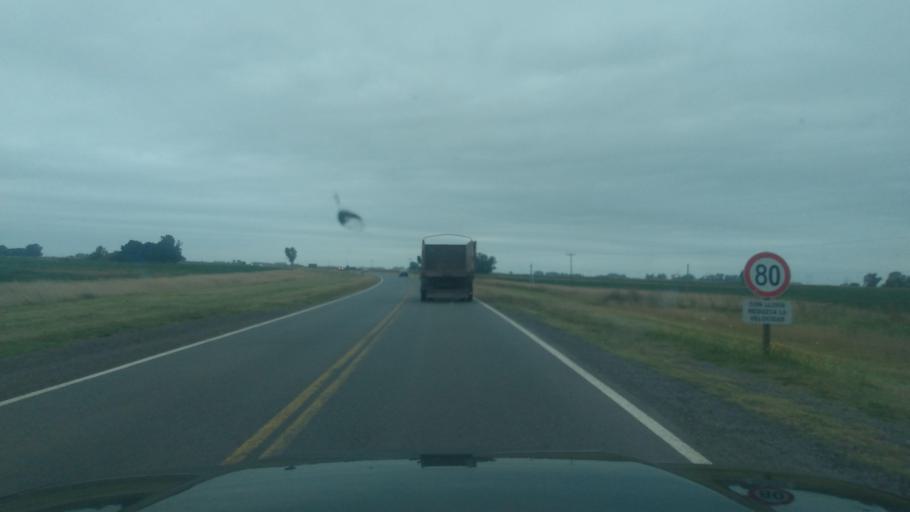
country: AR
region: Buenos Aires
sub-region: Partido de Nueve de Julio
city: Nueve de Julio
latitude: -35.3966
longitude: -60.7454
